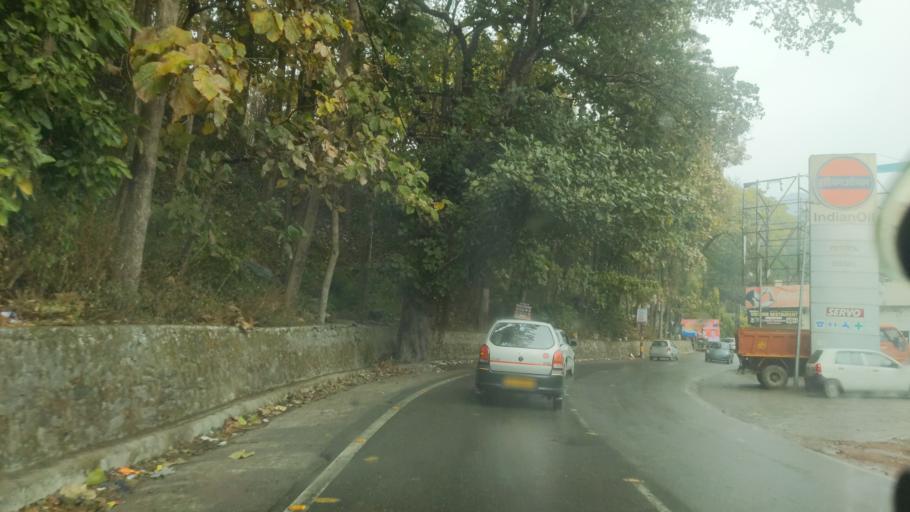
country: IN
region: Uttarakhand
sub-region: Naini Tal
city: Haldwani
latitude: 29.2815
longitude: 79.5448
